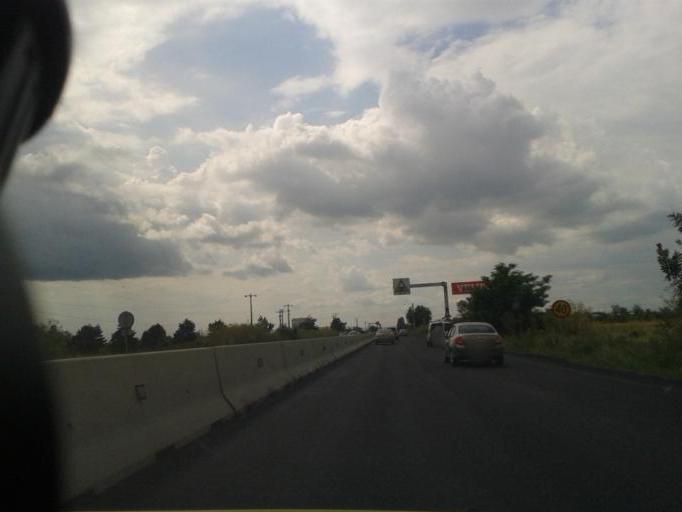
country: RO
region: Prahova
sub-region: Comuna Paulesti
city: Gageni
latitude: 44.9838
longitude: 25.9274
